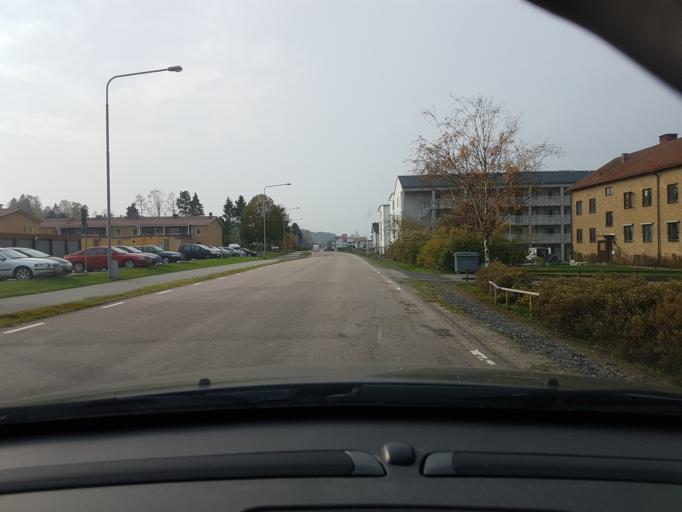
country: SE
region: Vaestra Goetaland
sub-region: Ale Kommun
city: Alvangen
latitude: 57.9614
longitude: 12.1301
